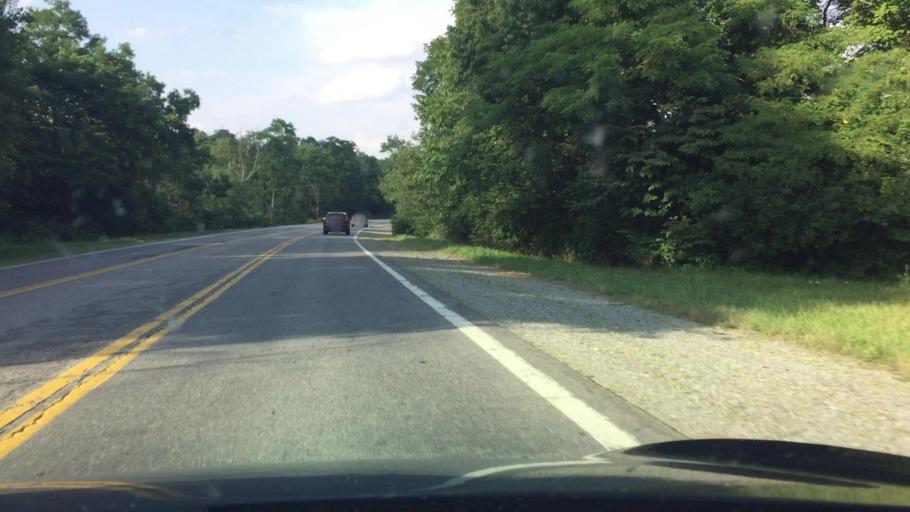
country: US
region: Virginia
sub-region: Pulaski County
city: Dublin
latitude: 37.1259
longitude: -80.6497
